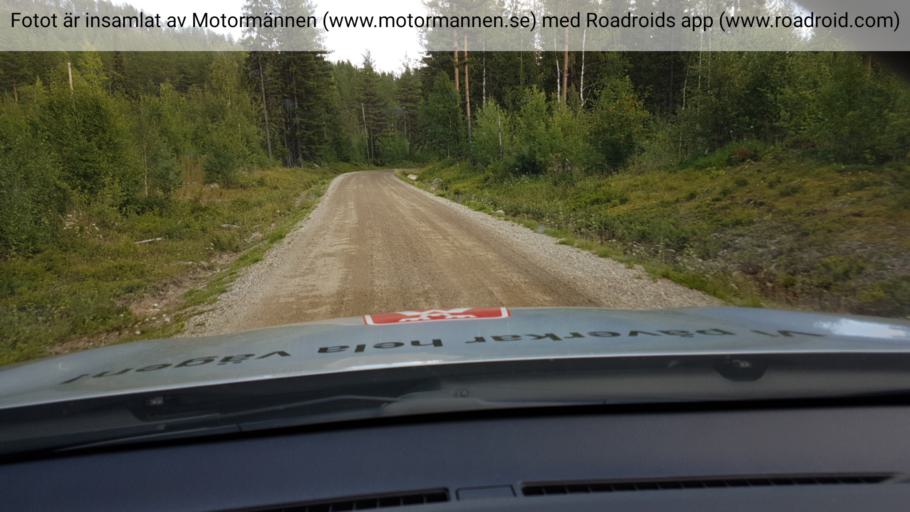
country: SE
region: Jaemtland
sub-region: Ragunda Kommun
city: Hammarstrand
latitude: 63.3461
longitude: 15.9786
